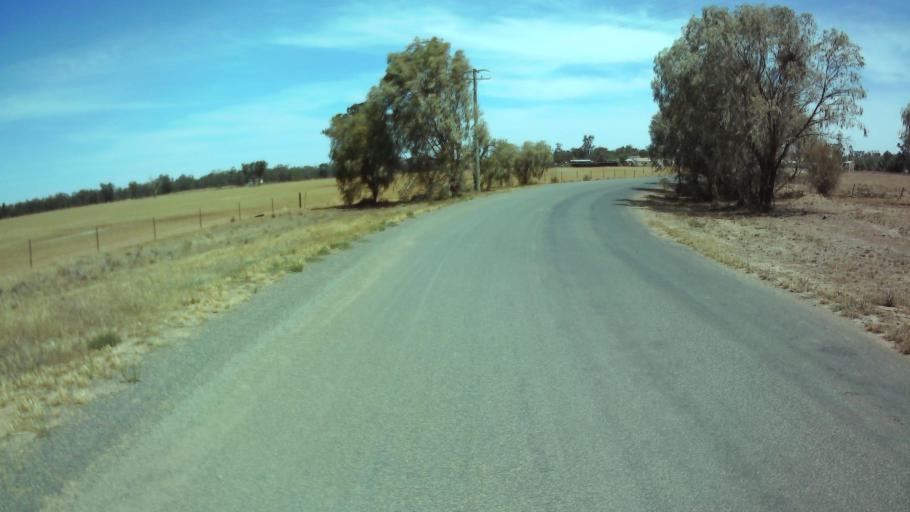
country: AU
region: New South Wales
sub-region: Weddin
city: Grenfell
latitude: -33.8364
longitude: 147.7466
